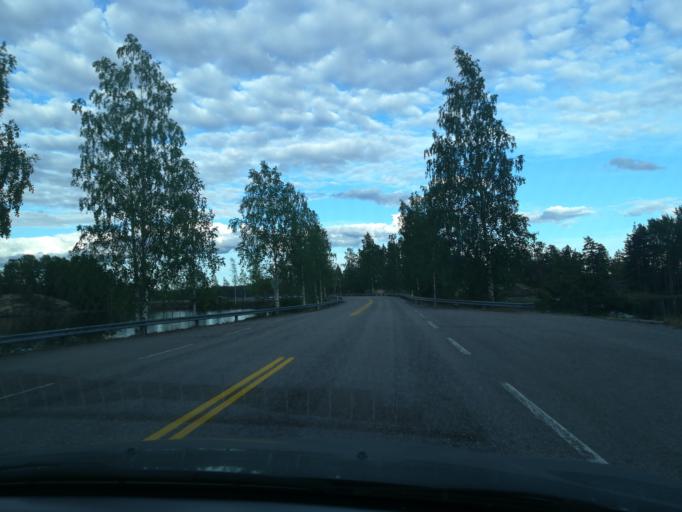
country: FI
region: Southern Savonia
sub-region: Mikkeli
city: Puumala
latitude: 61.5614
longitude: 27.9818
